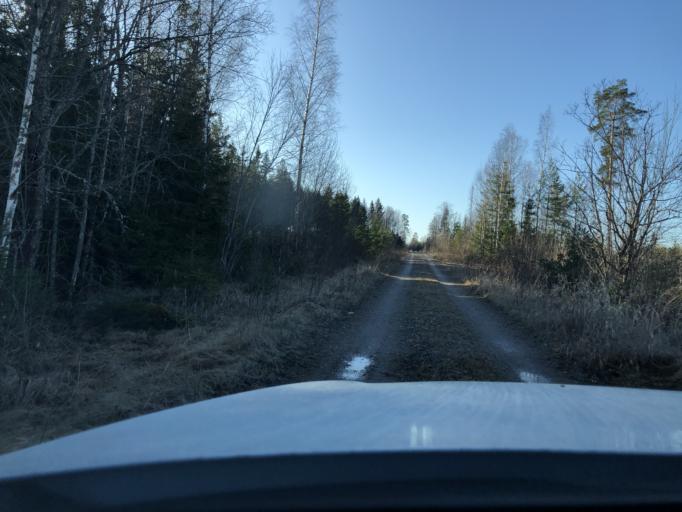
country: SE
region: Gaevleborg
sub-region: Gavle Kommun
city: Hedesunda
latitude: 60.3025
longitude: 16.8934
